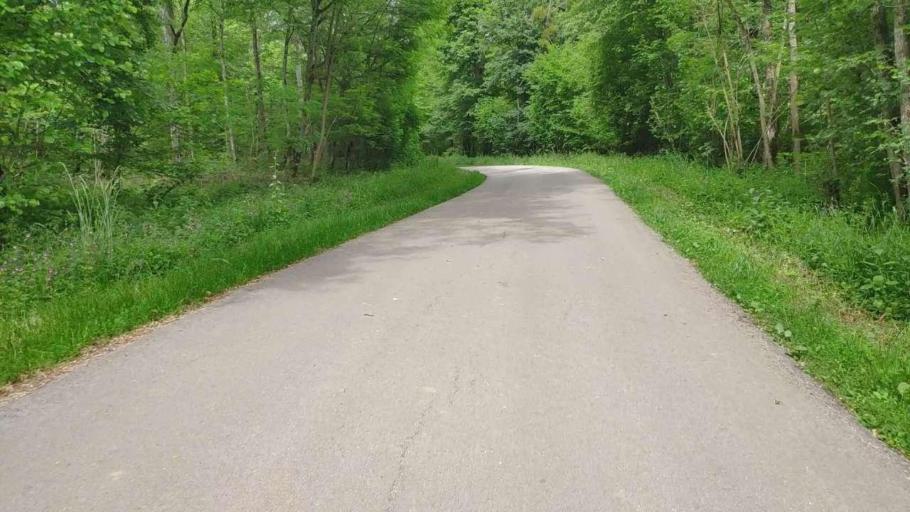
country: FR
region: Franche-Comte
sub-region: Departement du Jura
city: Montmorot
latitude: 46.7467
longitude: 5.5333
